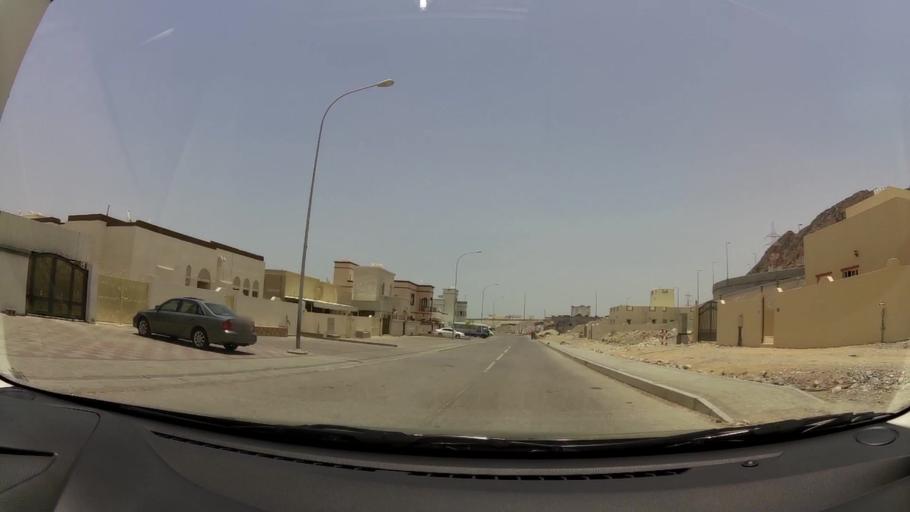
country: OM
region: Muhafazat Masqat
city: Bawshar
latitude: 23.5659
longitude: 58.4263
